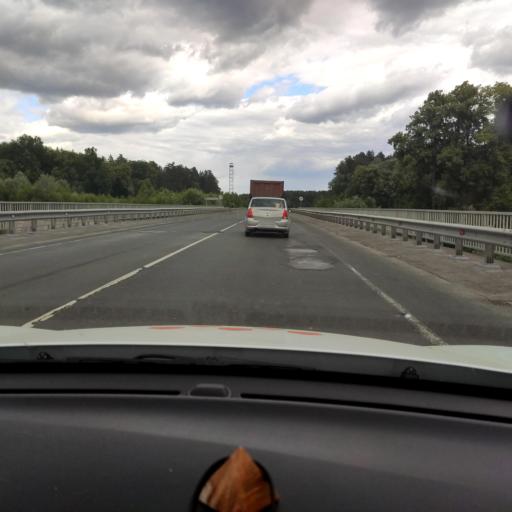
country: RU
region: Mariy-El
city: Yoshkar-Ola
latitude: 56.5422
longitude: 47.9698
